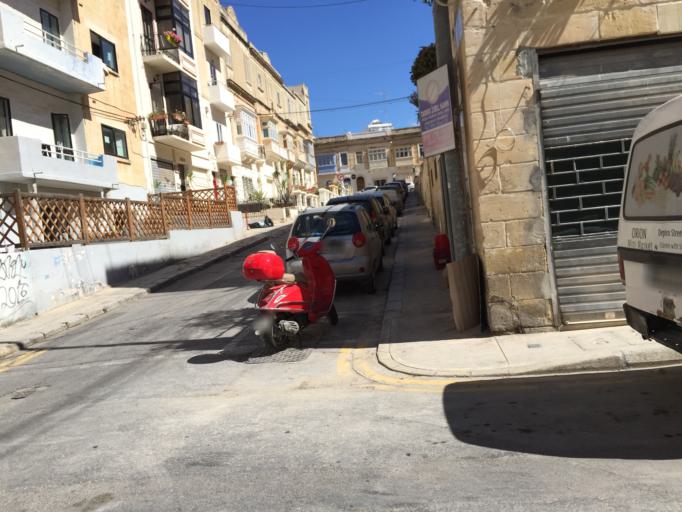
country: MT
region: Tas-Sliema
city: Sliema
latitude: 35.9127
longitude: 14.4964
